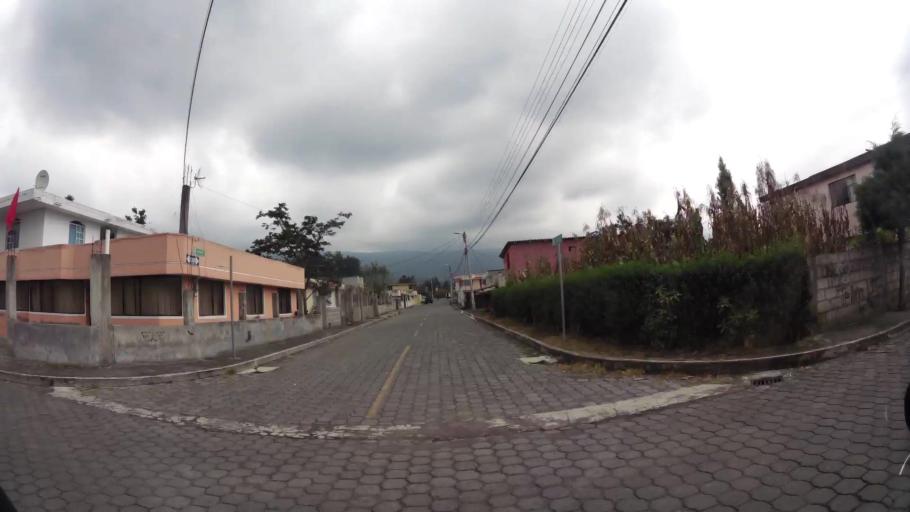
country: EC
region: Pichincha
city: Sangolqui
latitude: -0.3288
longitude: -78.4749
